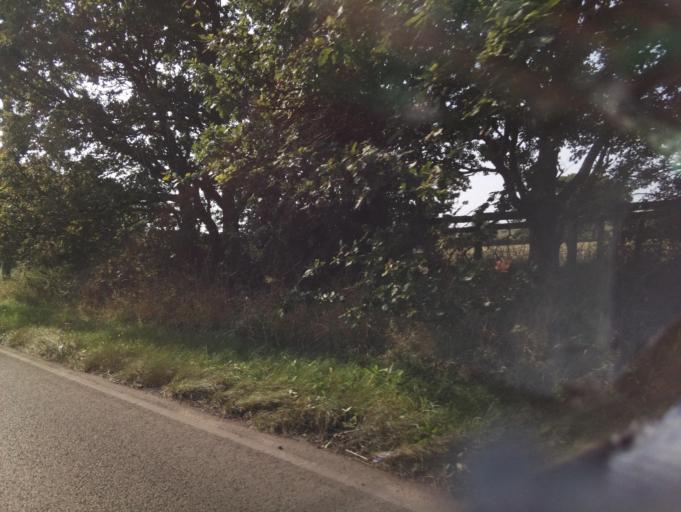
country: GB
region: England
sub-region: Walsall
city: Aldridge
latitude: 52.6197
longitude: -1.8910
